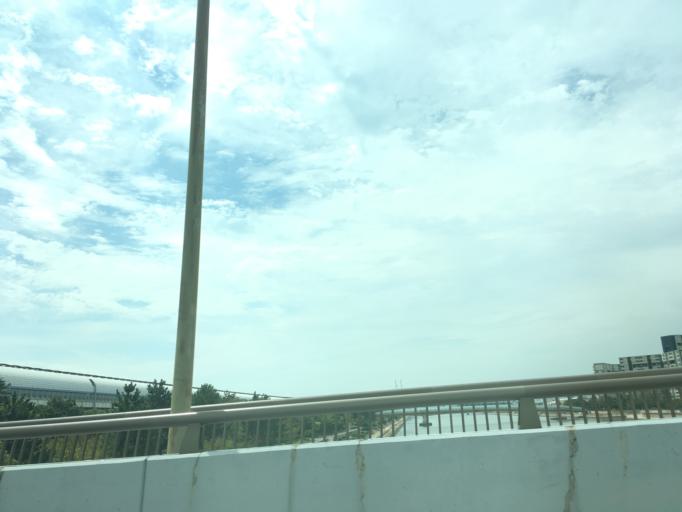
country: JP
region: Hyogo
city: Nishinomiya-hama
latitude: 34.7160
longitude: 135.3211
